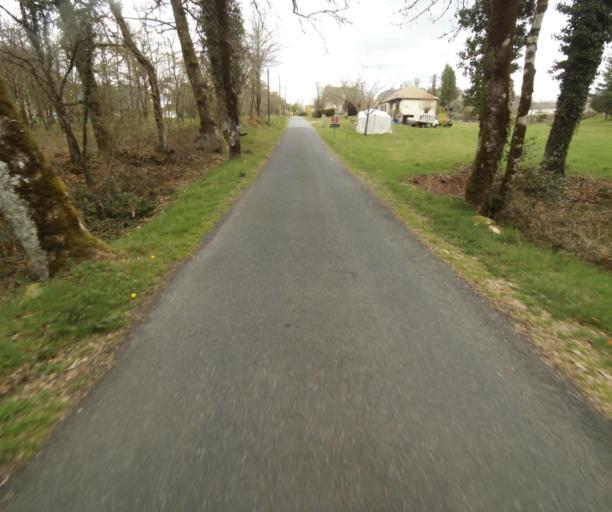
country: FR
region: Limousin
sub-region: Departement de la Correze
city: Correze
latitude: 45.3260
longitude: 1.9368
